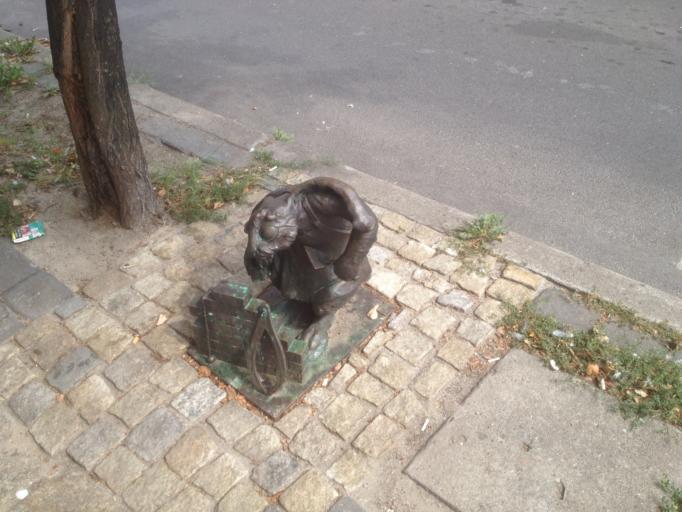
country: PL
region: Greater Poland Voivodeship
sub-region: Powiat gnieznienski
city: Gniezno
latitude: 52.5361
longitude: 17.5984
